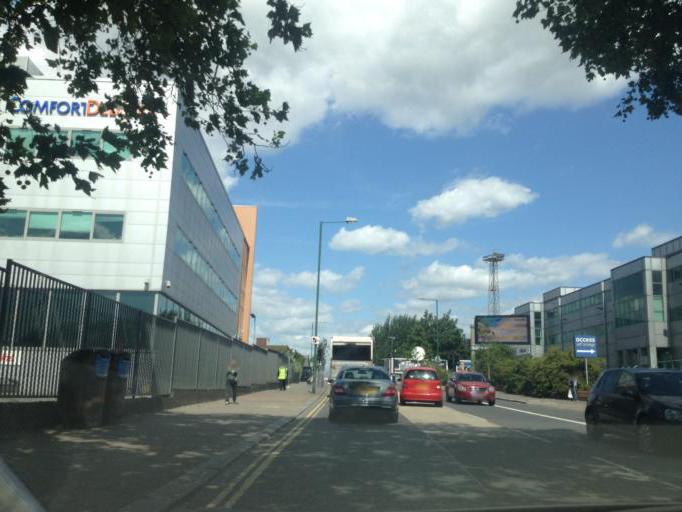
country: GB
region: England
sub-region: Greater London
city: Hendon
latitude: 51.5621
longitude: -0.2211
